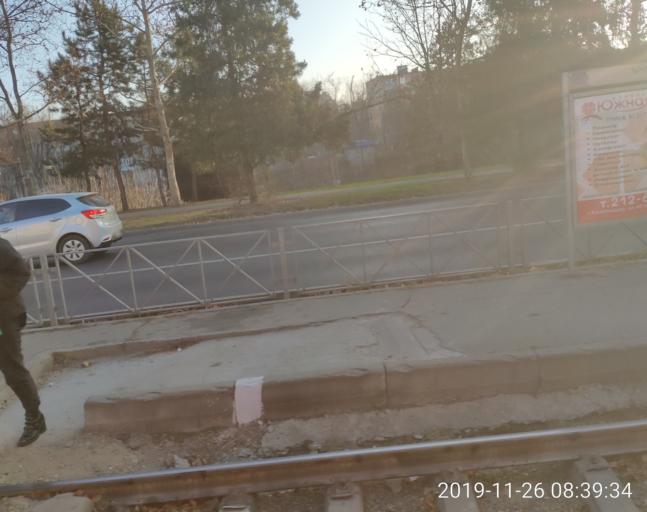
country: RU
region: Krasnodarskiy
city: Krasnodar
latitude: 45.0581
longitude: 38.9848
